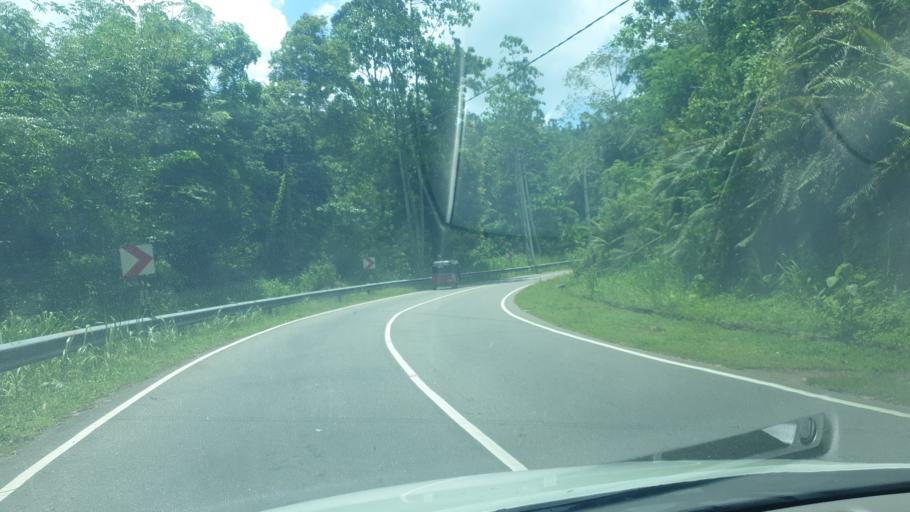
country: LK
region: Western
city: Horawala Junction
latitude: 6.5416
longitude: 80.2731
